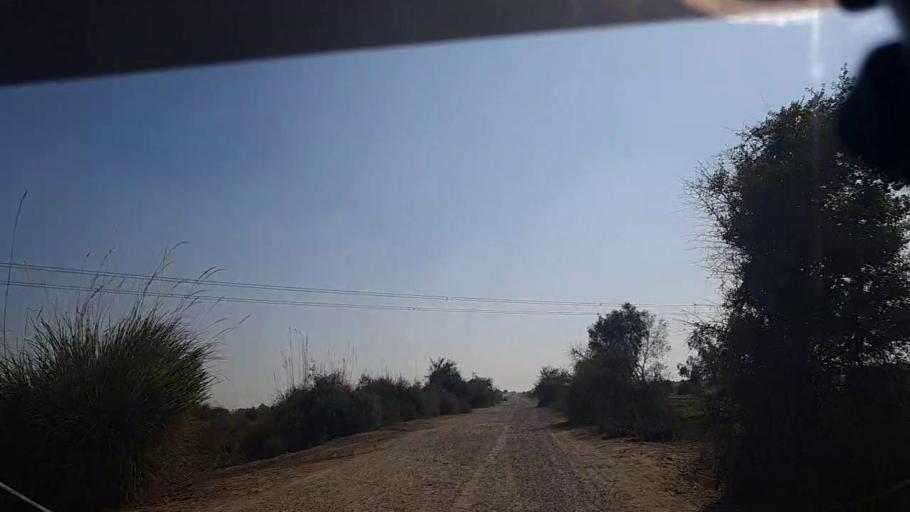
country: PK
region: Sindh
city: Khanpur
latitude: 27.5798
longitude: 69.3054
